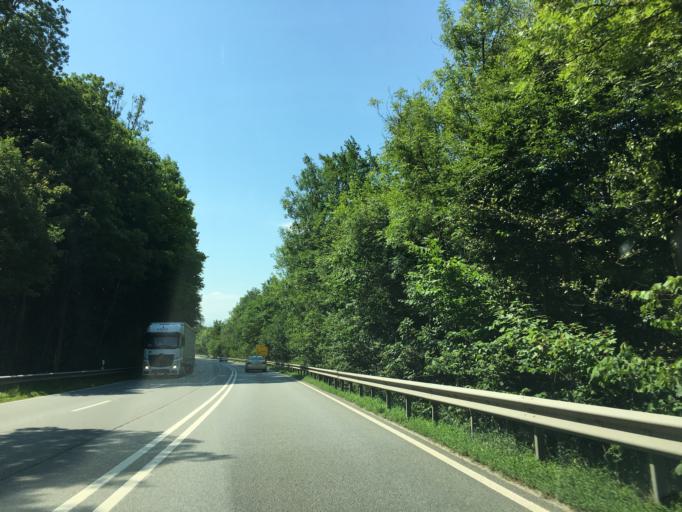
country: DE
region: Bavaria
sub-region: Upper Bavaria
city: Breitbrunn
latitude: 48.0261
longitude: 12.1733
